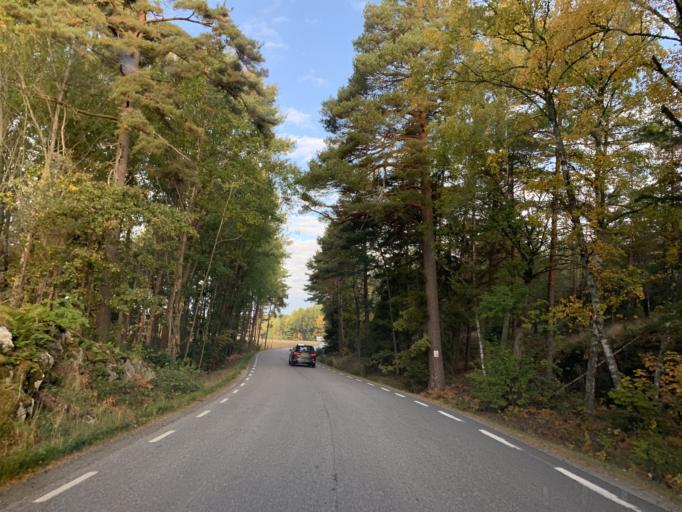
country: SE
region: Stockholm
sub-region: Upplands-Bro Kommun
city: Bro
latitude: 59.5058
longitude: 17.6062
